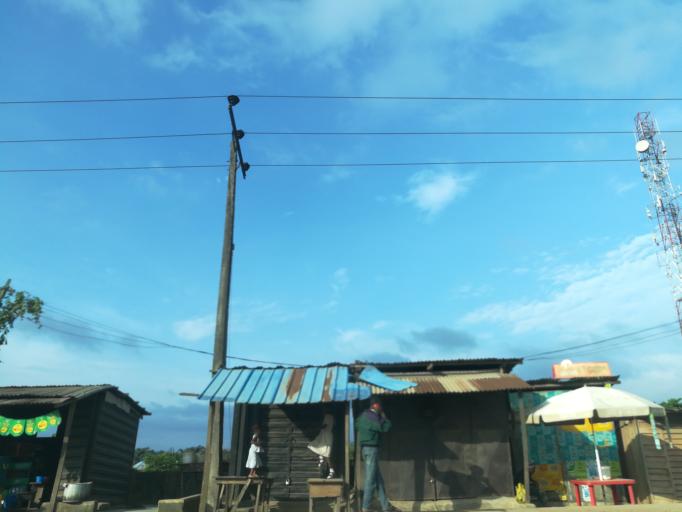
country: NG
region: Lagos
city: Ebute Ikorodu
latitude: 6.6114
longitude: 3.4828
